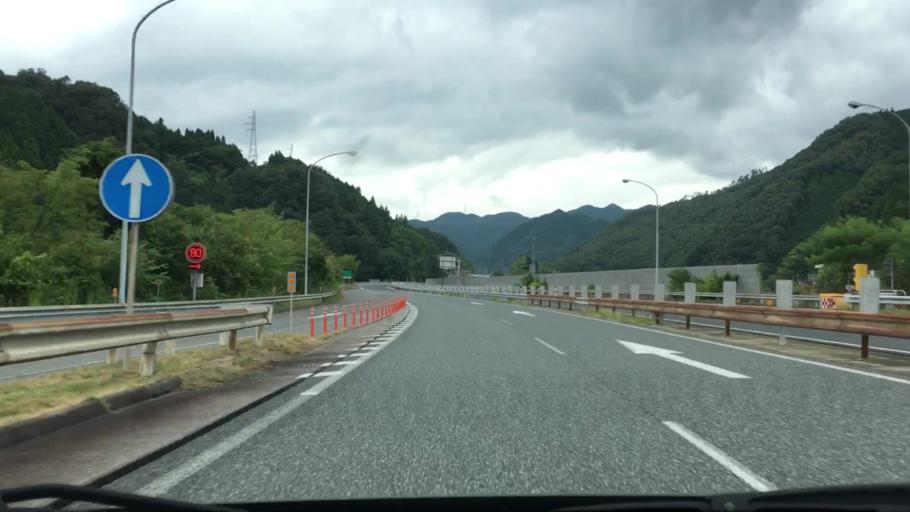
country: JP
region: Okayama
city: Niimi
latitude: 34.9991
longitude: 133.4461
